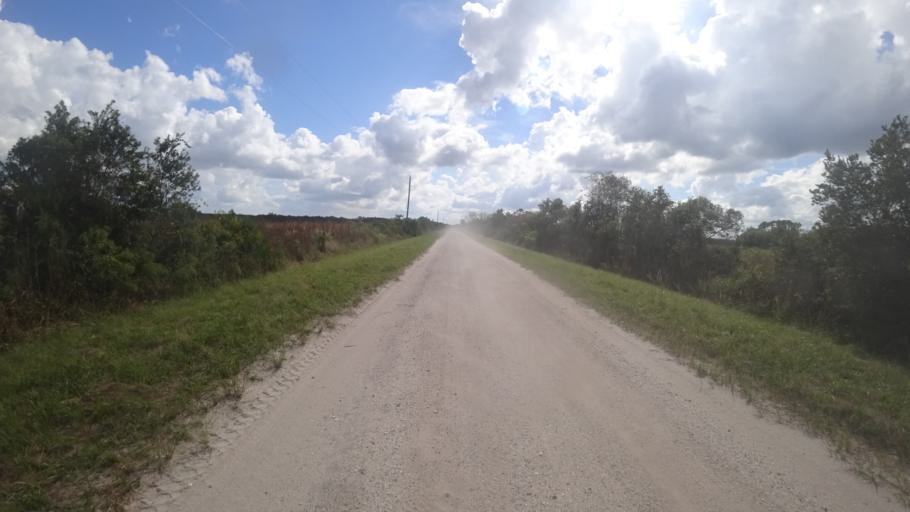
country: US
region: Florida
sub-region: Hillsborough County
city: Wimauma
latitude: 27.5675
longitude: -82.1742
